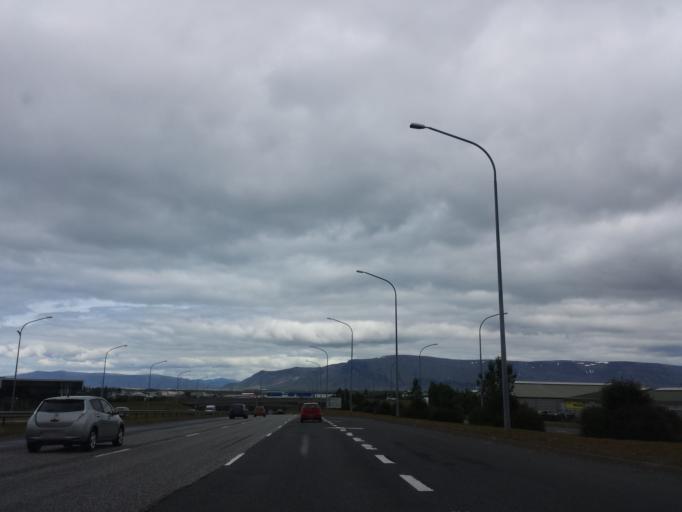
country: IS
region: Capital Region
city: Reykjavik
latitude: 64.1109
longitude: -21.8440
